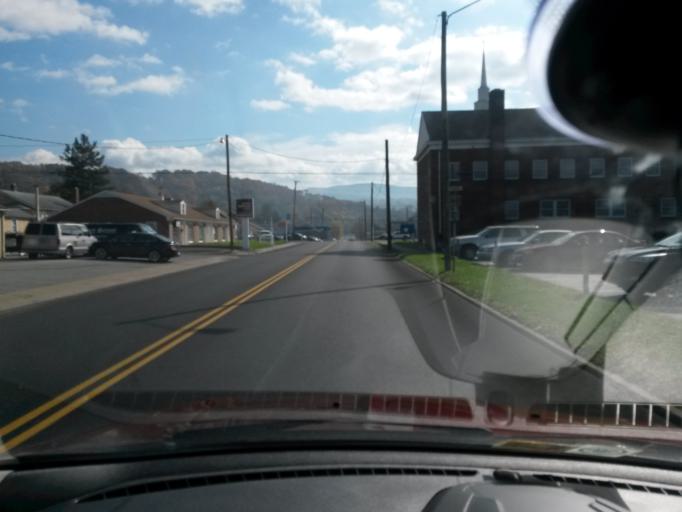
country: US
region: Virginia
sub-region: City of Covington
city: Covington
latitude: 37.7884
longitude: -79.9895
